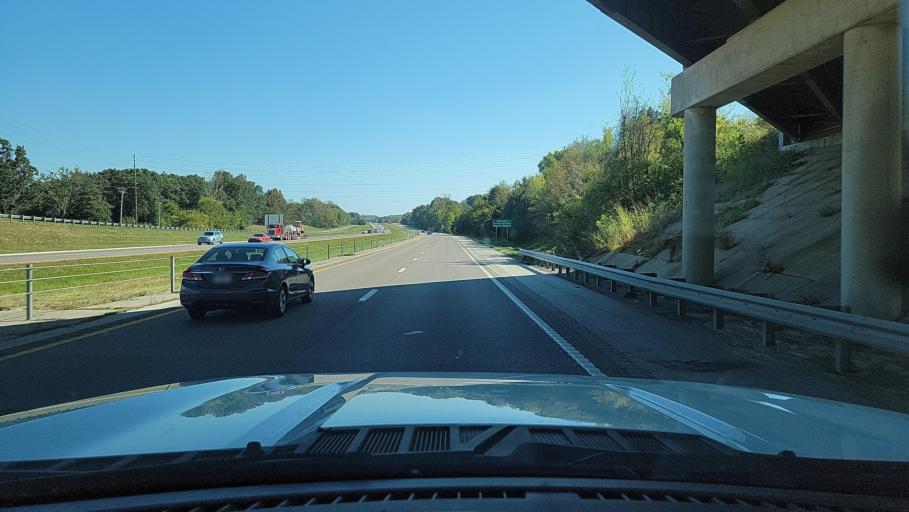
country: US
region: Missouri
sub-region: Jefferson County
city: Festus
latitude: 38.1921
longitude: -90.3958
